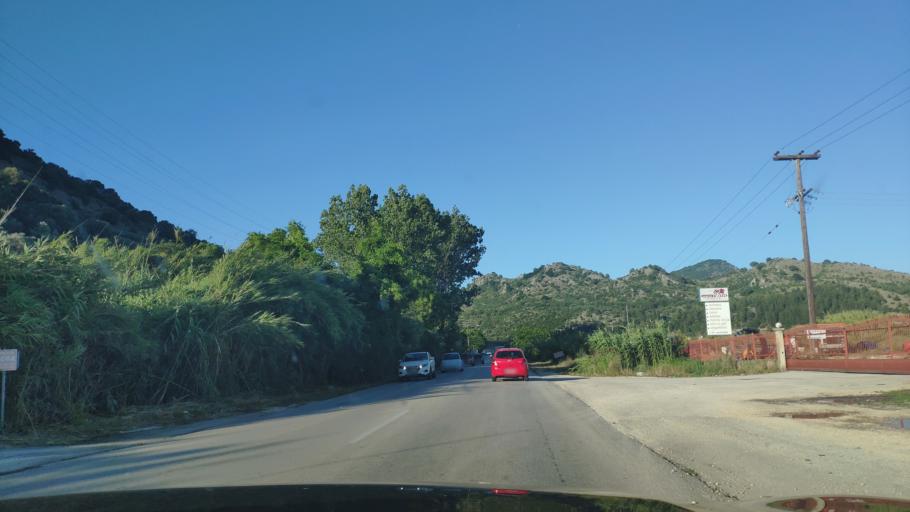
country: GR
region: Epirus
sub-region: Nomos Prevezis
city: Louros
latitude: 39.1782
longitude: 20.7789
